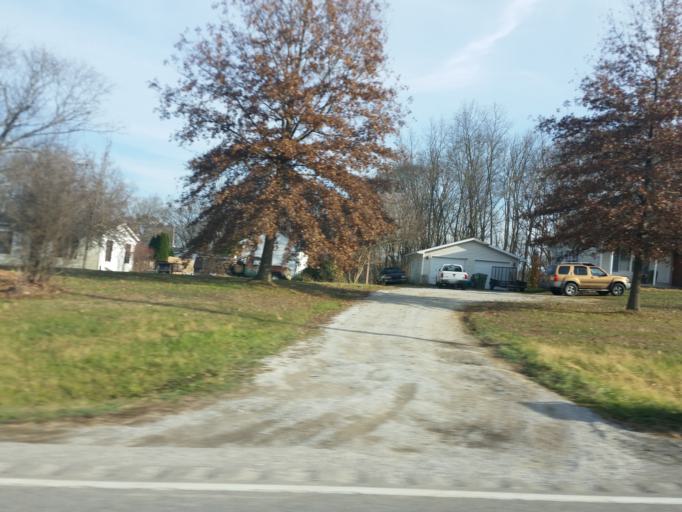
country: US
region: Kentucky
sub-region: Pendleton County
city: Falmouth
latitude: 38.7803
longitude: -84.3506
